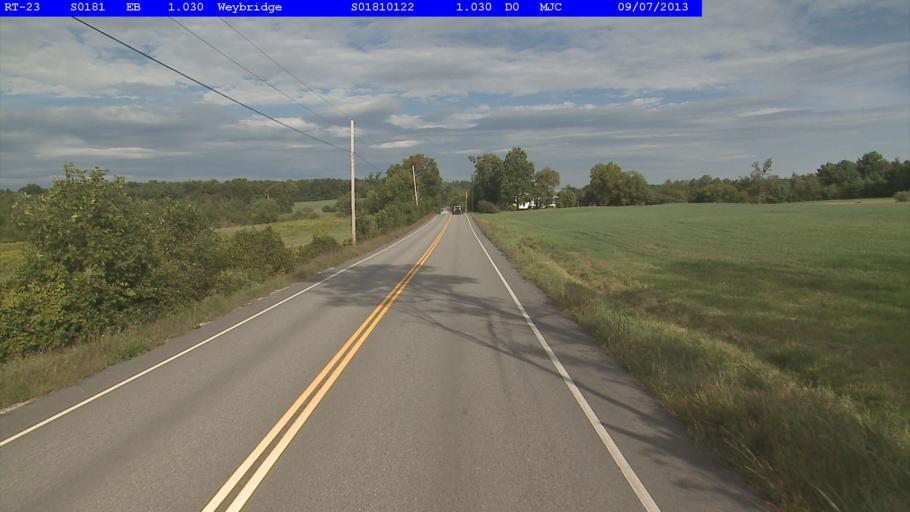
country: US
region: Vermont
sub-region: Addison County
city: Middlebury (village)
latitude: 44.0282
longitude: -73.1986
